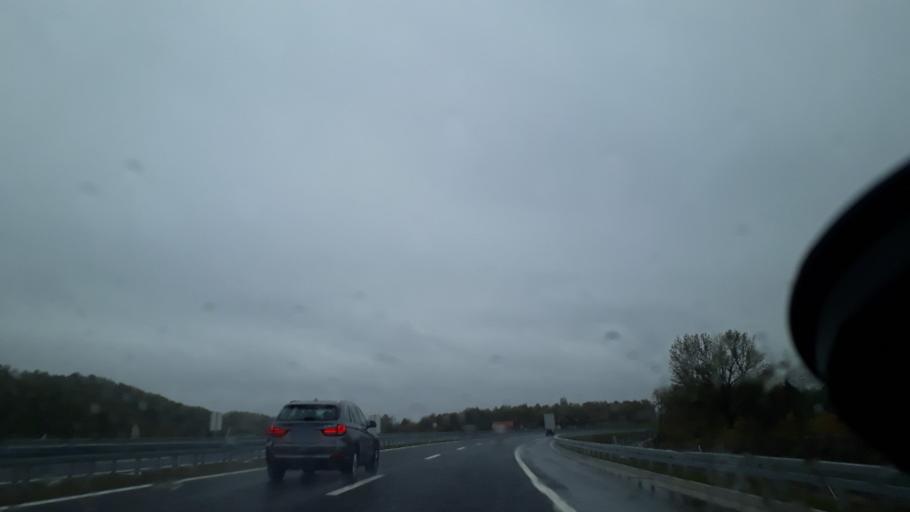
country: BA
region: Republika Srpska
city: Maglajani
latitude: 44.8728
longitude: 17.3922
